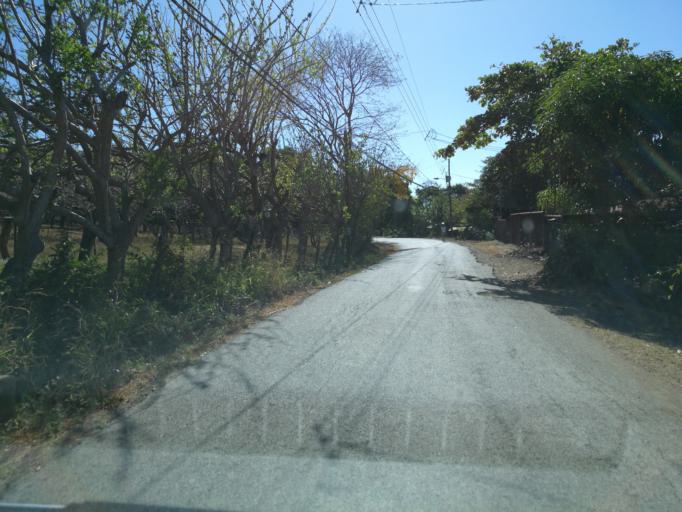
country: CR
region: Puntarenas
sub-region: Canton Central de Puntarenas
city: Puntarenas
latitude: 10.0928
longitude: -84.9725
